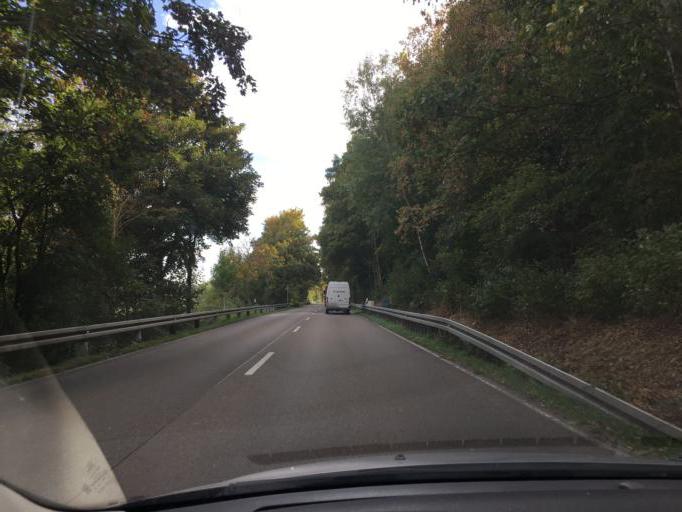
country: DE
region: Saxony
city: Meissen
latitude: 51.1816
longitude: 13.4516
